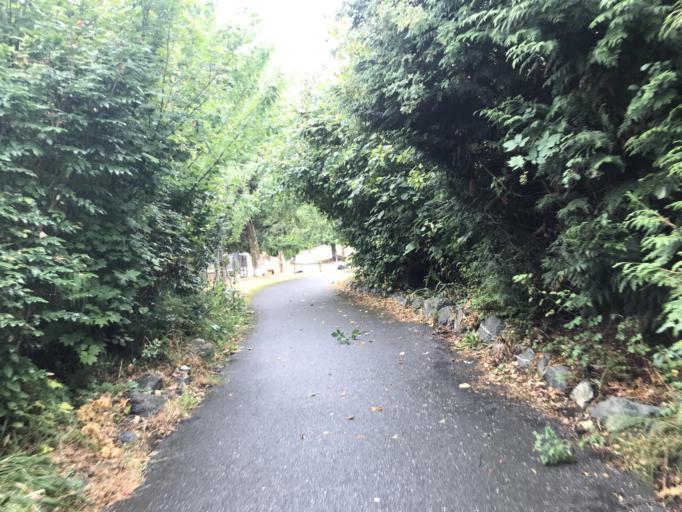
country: US
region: Washington
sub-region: Whatcom County
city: Bellingham
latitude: 48.7571
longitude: -122.4874
